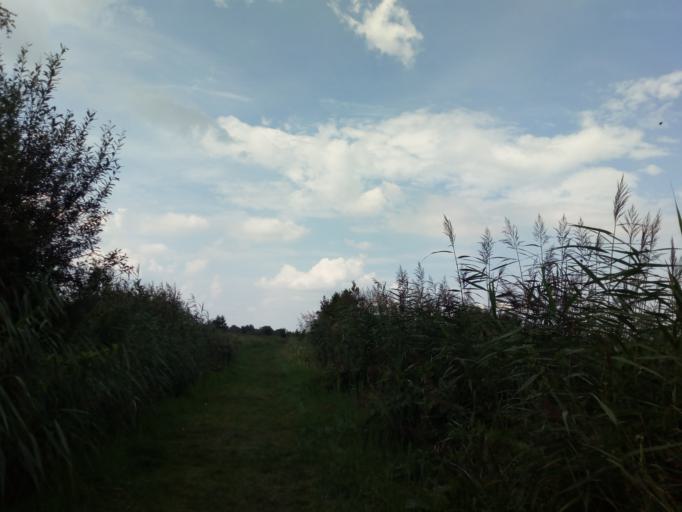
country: NL
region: Friesland
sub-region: Gemeente Smallingerland
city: Oudega
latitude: 53.1197
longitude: 5.9523
